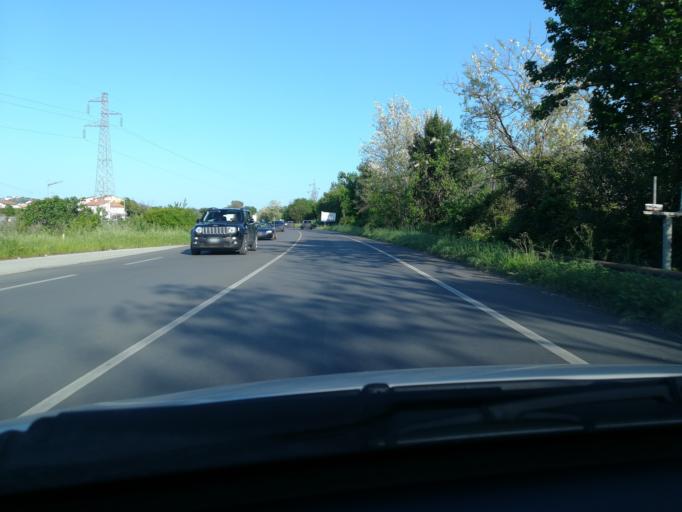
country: IT
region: Emilia-Romagna
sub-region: Provincia di Rimini
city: Montalbano
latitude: 43.9591
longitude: 12.7170
